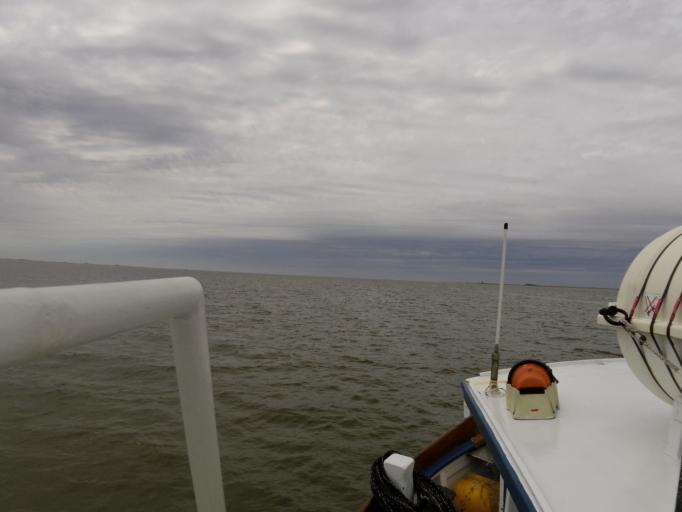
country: DE
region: Schleswig-Holstein
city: Langeness
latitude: 54.6129
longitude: 8.6068
